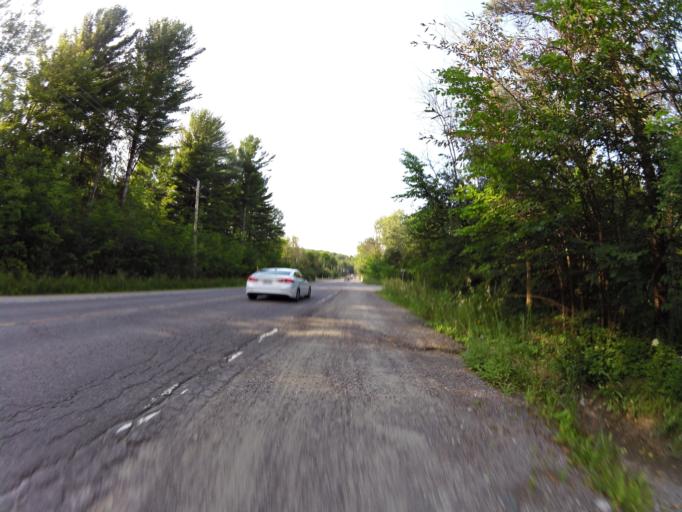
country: CA
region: Quebec
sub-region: Outaouais
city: Gatineau
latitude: 45.4951
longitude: -75.8139
